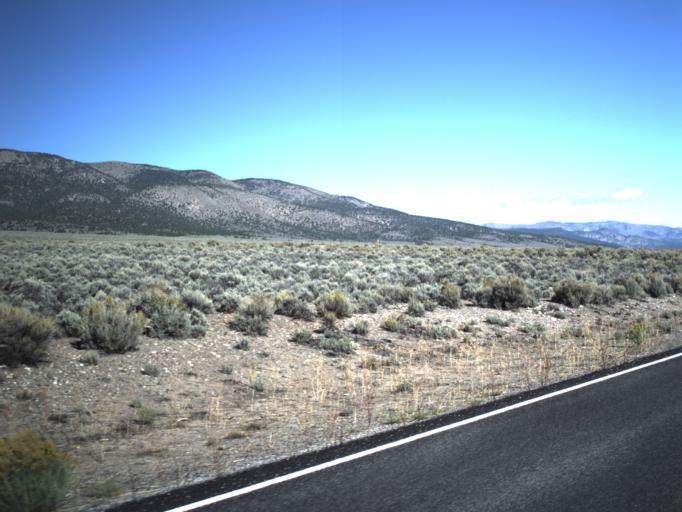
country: US
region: Utah
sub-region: Piute County
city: Junction
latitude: 38.1996
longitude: -112.0085
